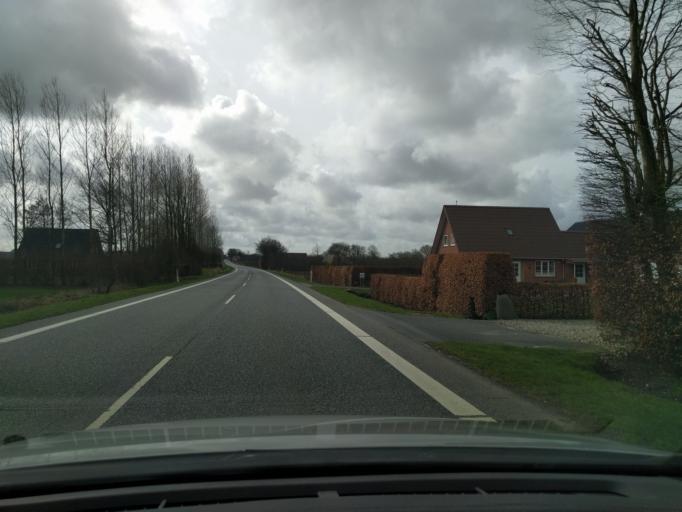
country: DK
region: South Denmark
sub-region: Tonder Kommune
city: Toftlund
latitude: 55.1458
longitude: 9.0185
